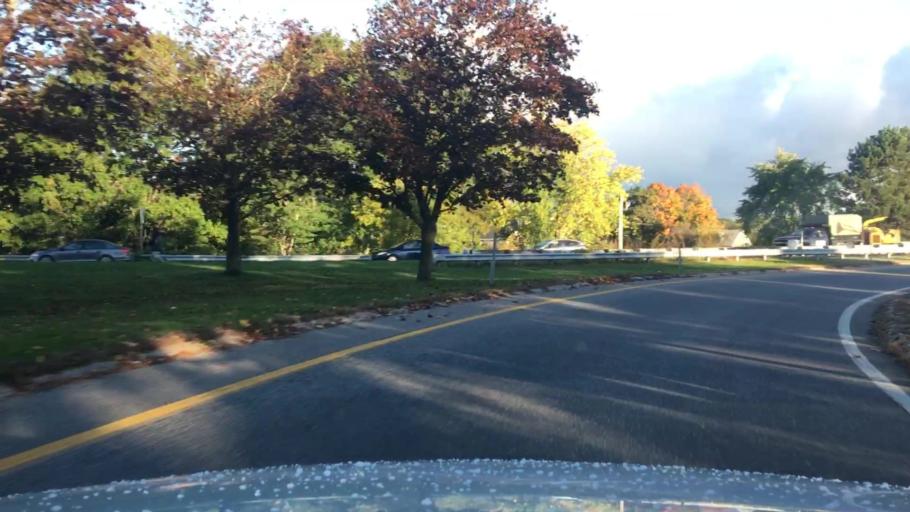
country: US
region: Maine
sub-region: Cumberland County
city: Portland
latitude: 43.6563
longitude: -70.2863
